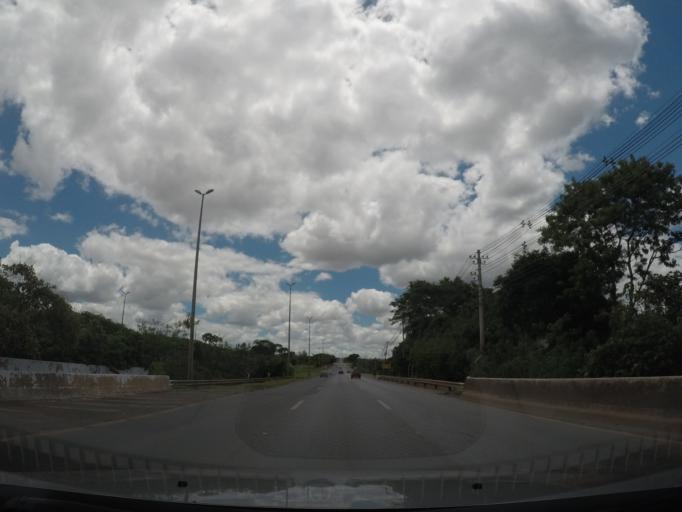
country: BR
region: Federal District
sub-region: Brasilia
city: Brasilia
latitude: -15.7284
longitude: -47.9098
